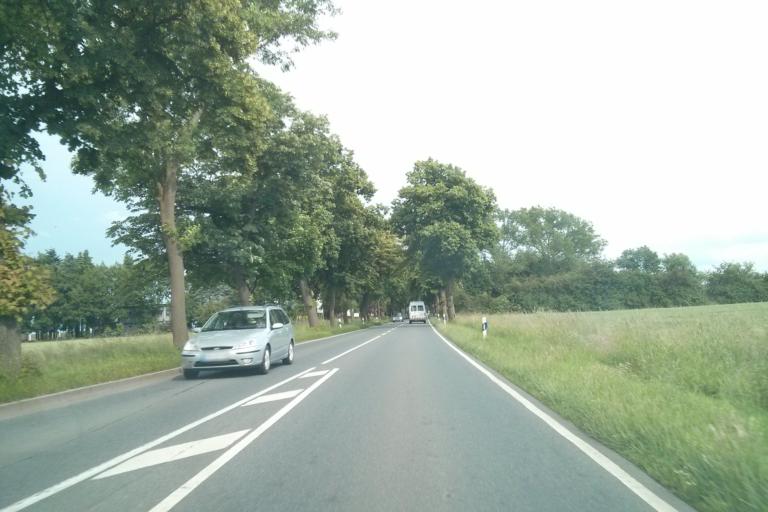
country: DE
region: Lower Saxony
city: Ahsen-Oetzen
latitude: 52.9642
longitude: 9.0589
